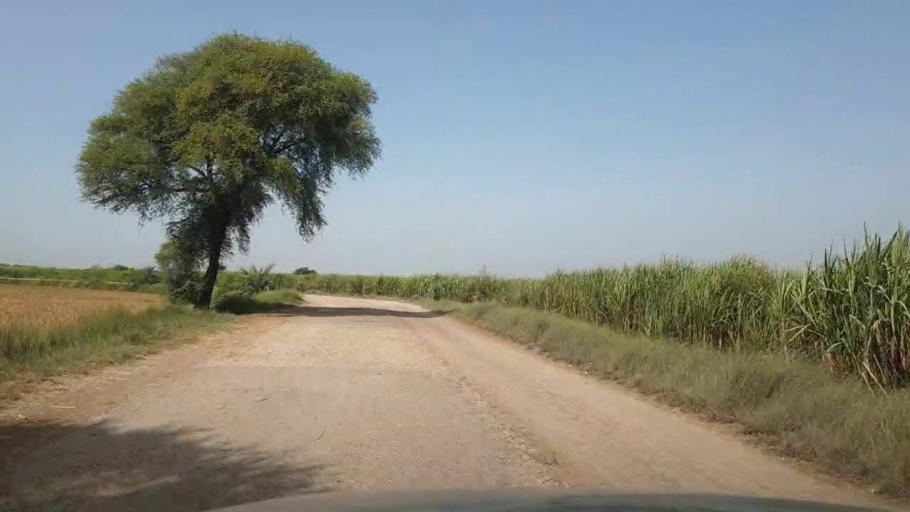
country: PK
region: Sindh
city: Tando Muhammad Khan
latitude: 25.1571
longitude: 68.4038
